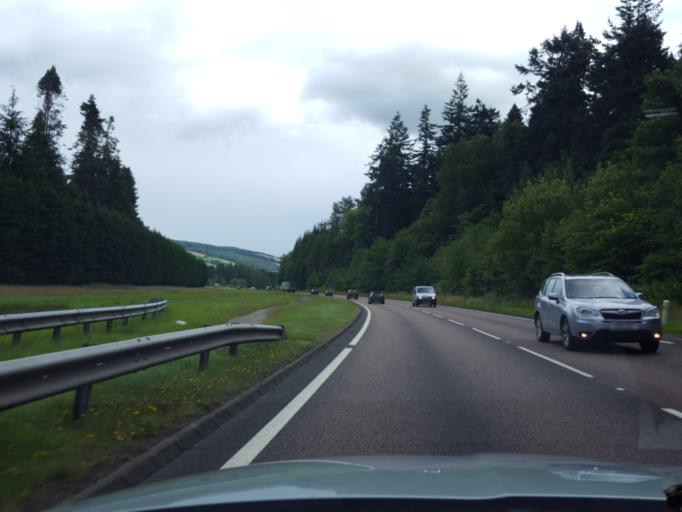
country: GB
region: Scotland
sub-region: Perth and Kinross
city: Pitlochry
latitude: 56.6977
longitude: -3.7450
